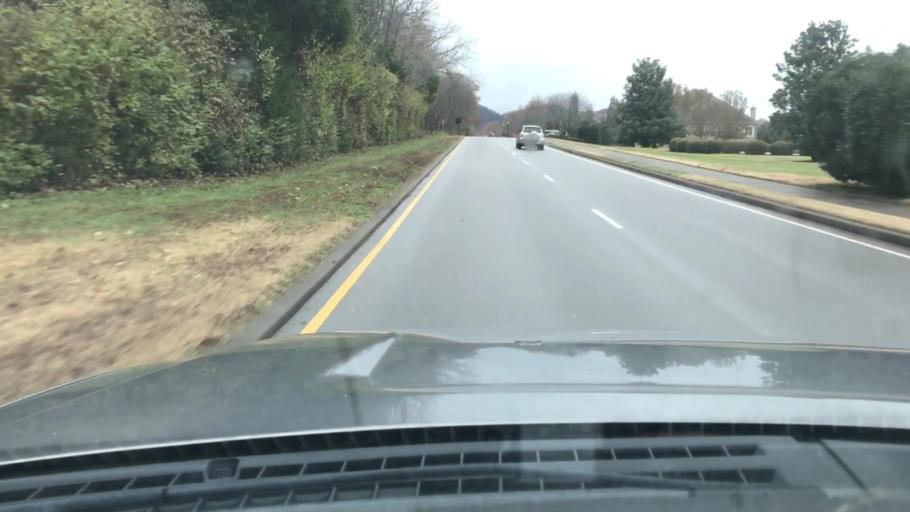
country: US
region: Tennessee
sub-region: Williamson County
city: Brentwood Estates
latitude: 36.0135
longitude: -86.8031
